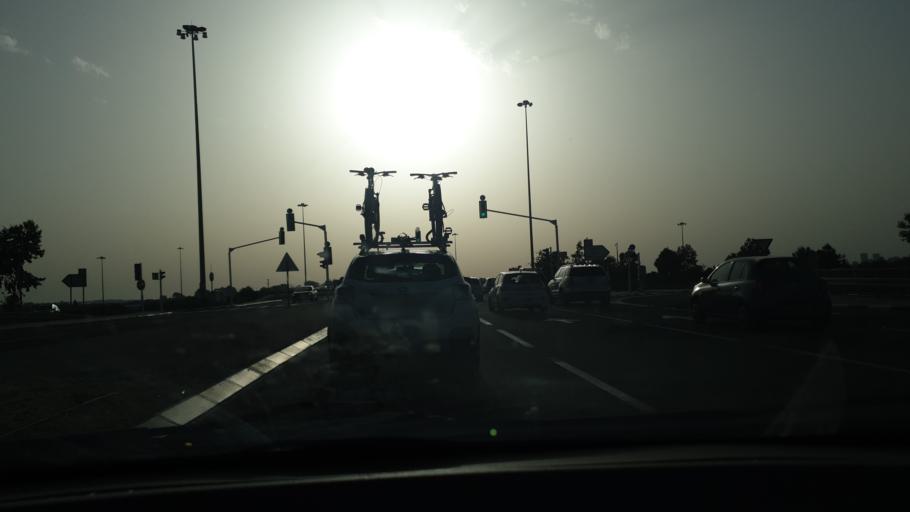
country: IL
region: Central District
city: Even Yehuda
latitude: 32.2558
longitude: 34.8944
